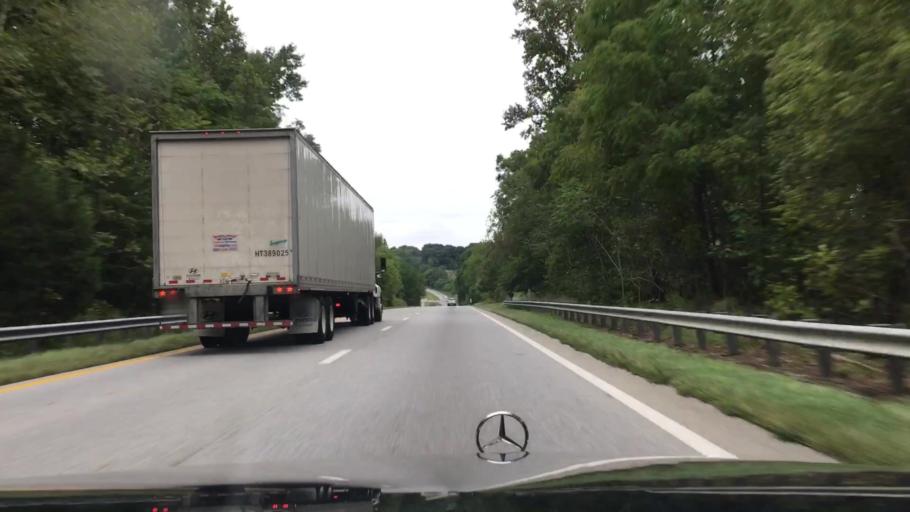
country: US
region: Virginia
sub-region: Amherst County
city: Amherst
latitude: 37.6101
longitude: -79.0210
